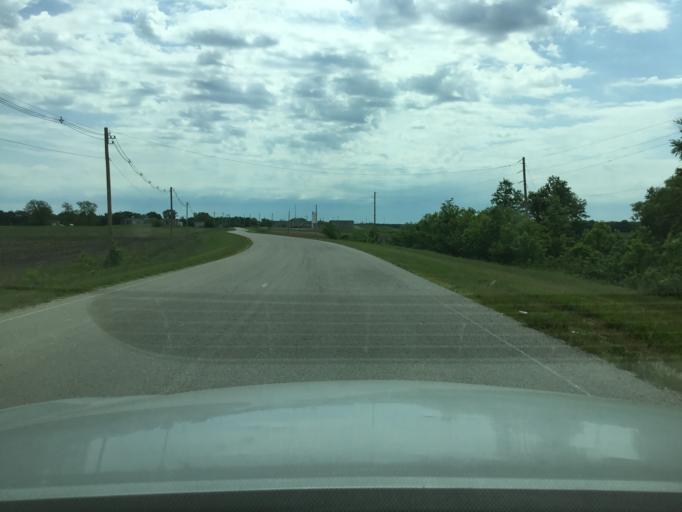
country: US
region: Kansas
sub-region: Montgomery County
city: Coffeyville
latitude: 37.0073
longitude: -95.6149
